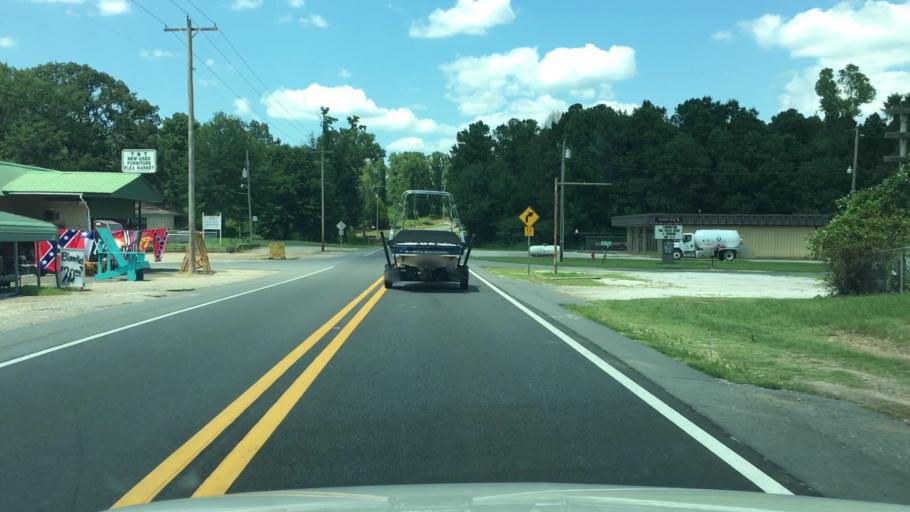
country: US
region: Arkansas
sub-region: Garland County
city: Lake Hamilton
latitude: 34.2837
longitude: -93.1631
